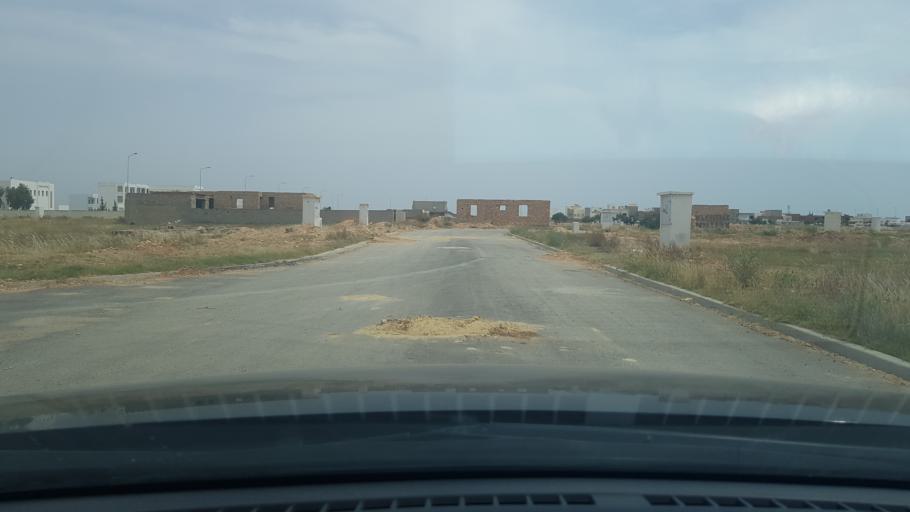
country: TN
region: Safaqis
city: Al Qarmadah
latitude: 34.8234
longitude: 10.7419
